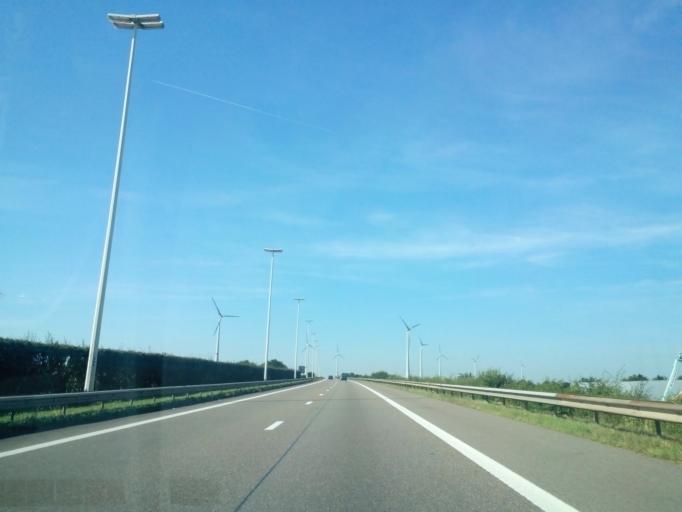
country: BE
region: Flanders
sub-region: Provincie Vlaams-Brabant
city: Diest
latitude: 50.9575
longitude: 5.0665
